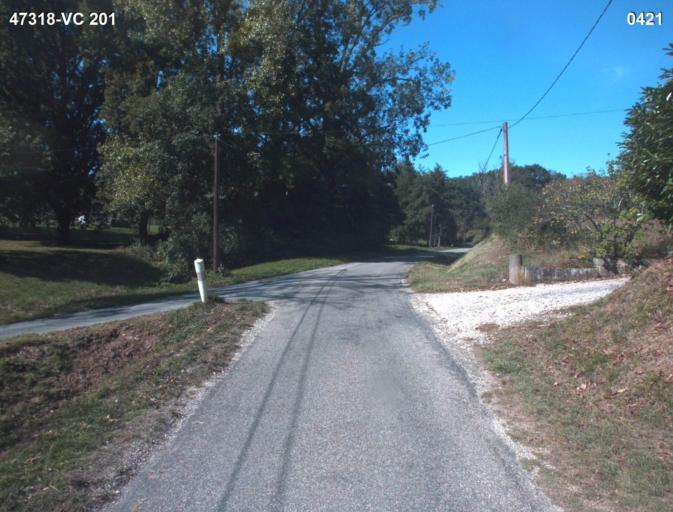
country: FR
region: Aquitaine
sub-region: Departement du Lot-et-Garonne
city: Vianne
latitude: 44.2016
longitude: 0.3198
